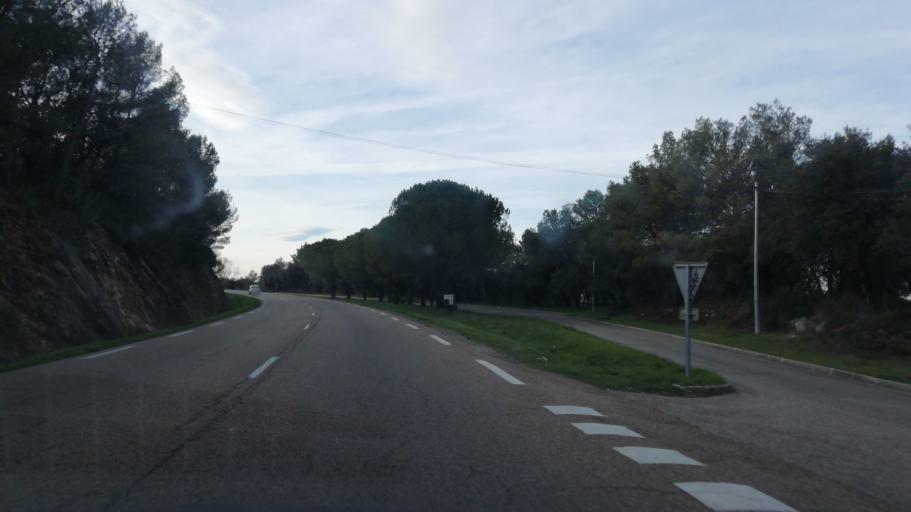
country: FR
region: Languedoc-Roussillon
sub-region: Departement du Gard
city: Caveirac
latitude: 43.8506
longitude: 4.2841
